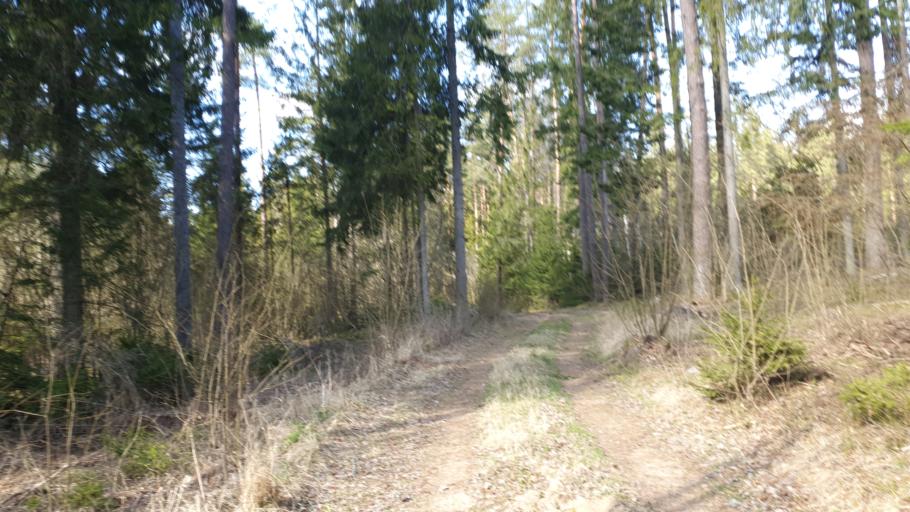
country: LT
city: Aukstadvaris
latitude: 54.4955
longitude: 24.6509
